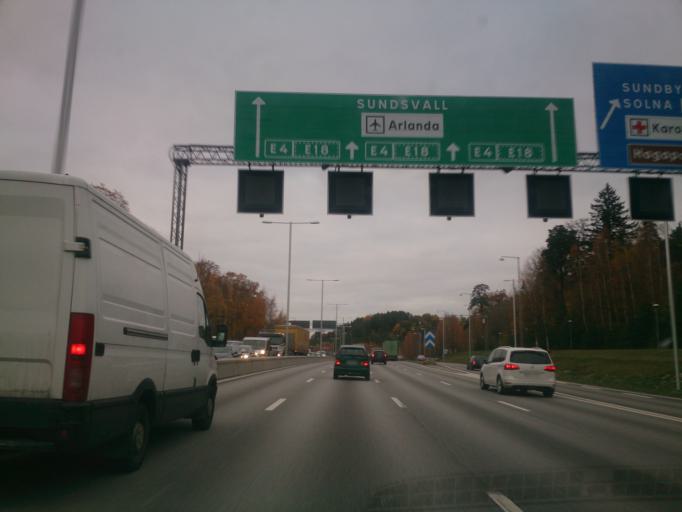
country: SE
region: Stockholm
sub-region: Norrtalje Kommun
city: Bergshamra
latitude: 59.3603
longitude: 18.0275
